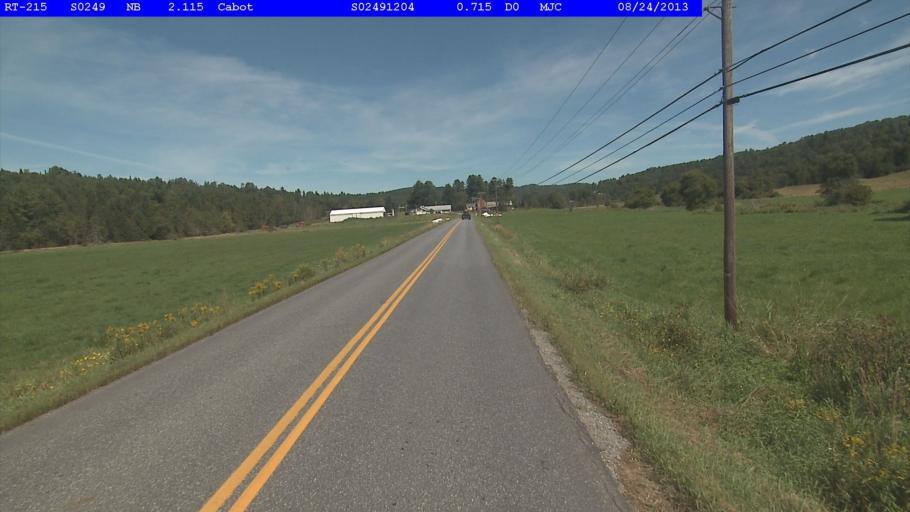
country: US
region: Vermont
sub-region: Caledonia County
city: Hardwick
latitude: 44.3776
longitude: -72.3348
